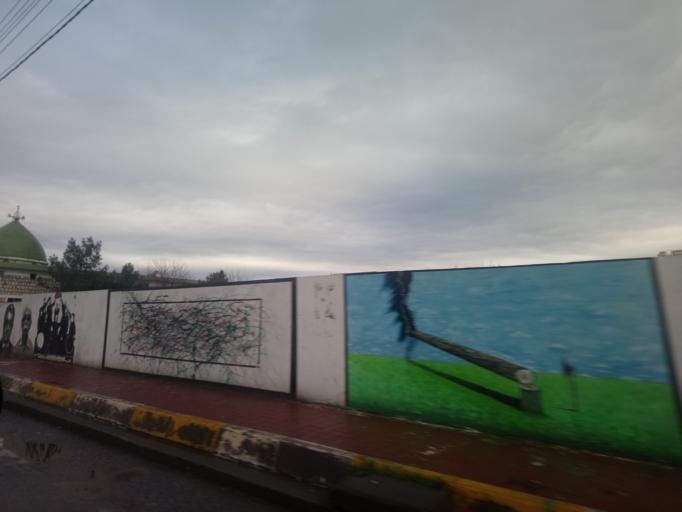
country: IQ
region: As Sulaymaniyah
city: Qeladize
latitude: 36.1849
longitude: 45.1185
